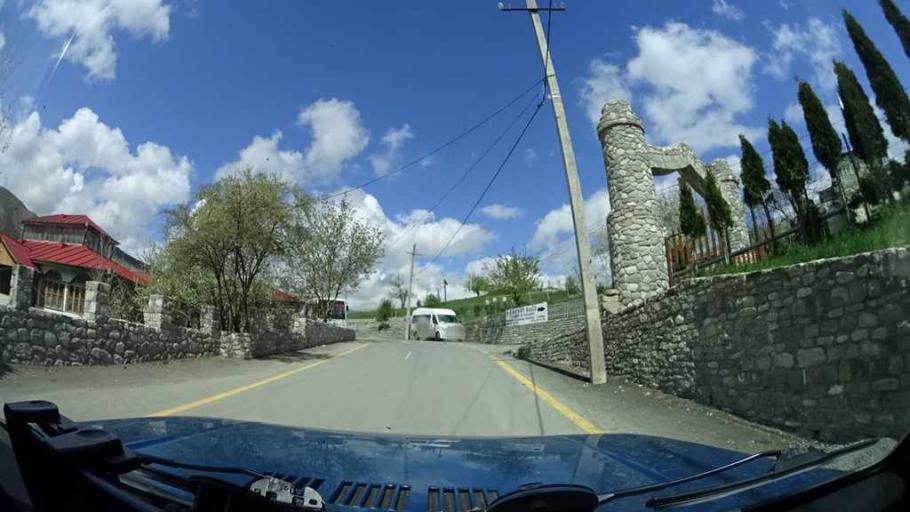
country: AZ
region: Ismayilli
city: Basqal
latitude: 40.8431
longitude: 48.3767
